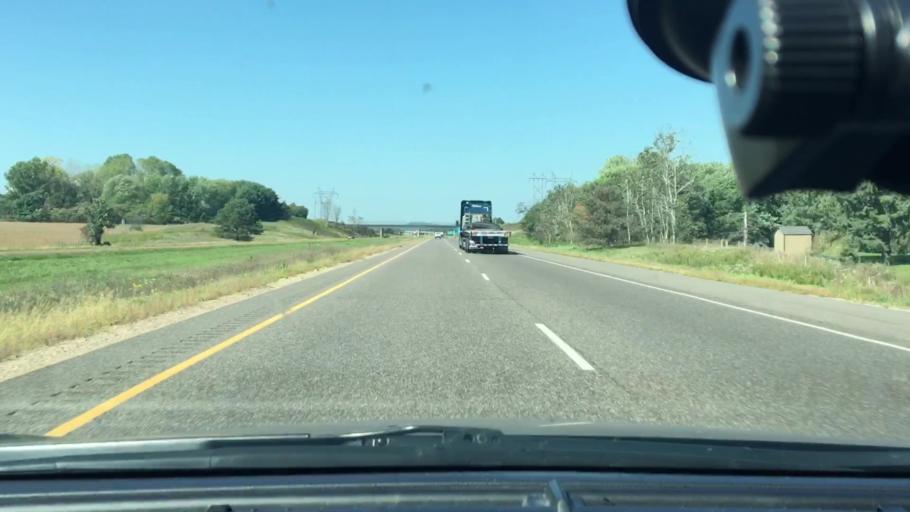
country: US
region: Wisconsin
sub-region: Eau Claire County
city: Eau Claire
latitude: 44.8346
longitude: -91.5839
